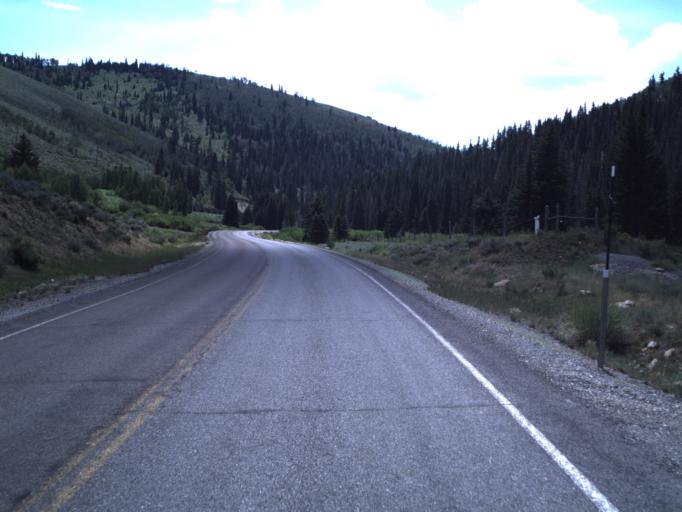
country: US
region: Utah
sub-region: Sanpete County
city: Fairview
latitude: 39.6948
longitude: -111.1567
